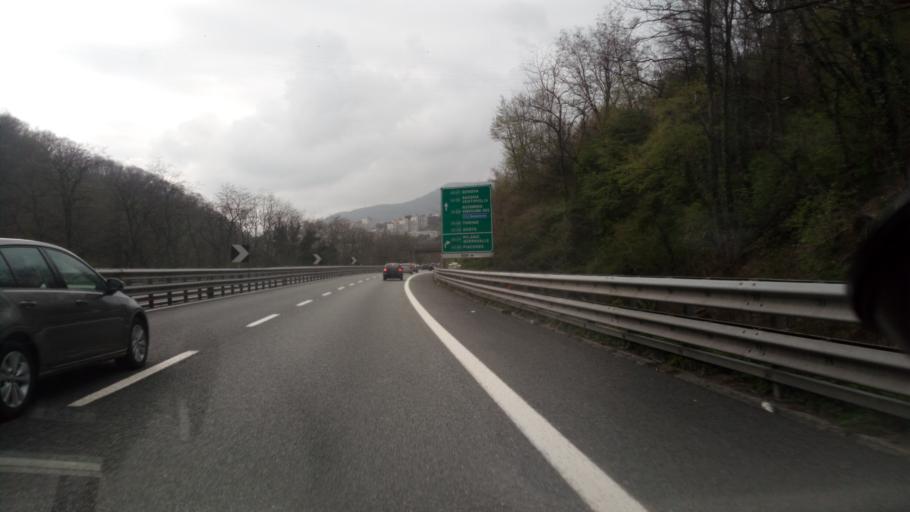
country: IT
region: Liguria
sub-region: Provincia di Genova
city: Genoa
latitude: 44.4457
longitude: 8.9151
